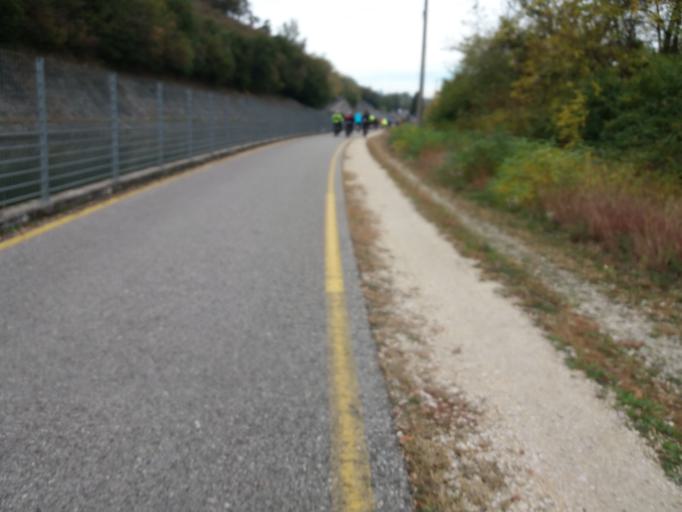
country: IT
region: Veneto
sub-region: Provincia di Verona
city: Pastrengo
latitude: 45.5018
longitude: 10.8036
